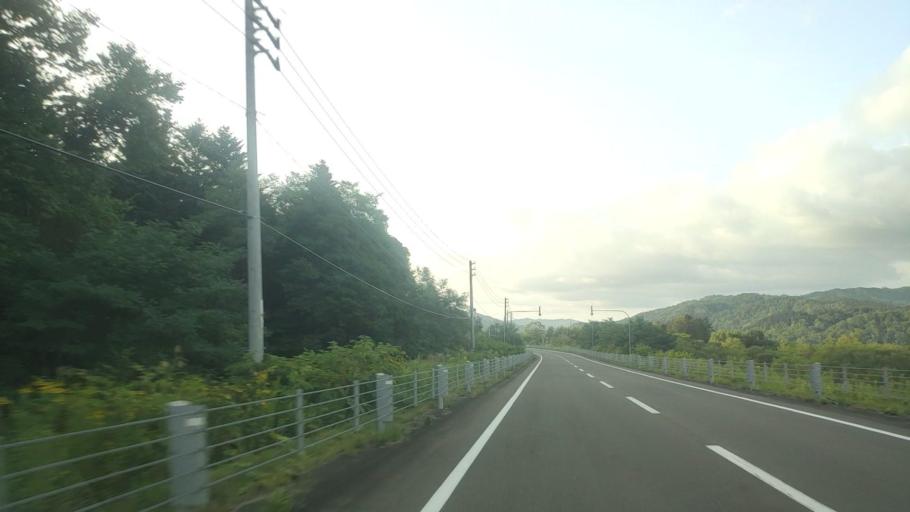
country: JP
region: Hokkaido
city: Bibai
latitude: 43.0762
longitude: 142.1020
